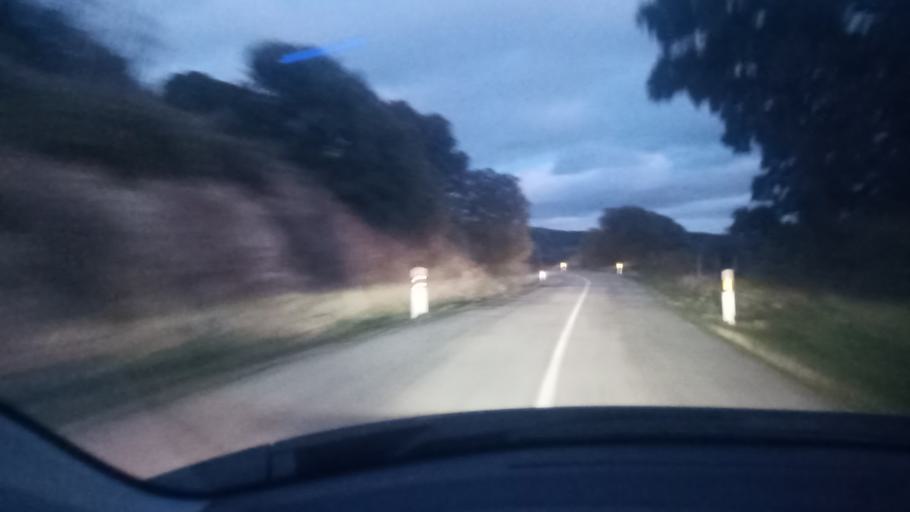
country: ES
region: Madrid
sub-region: Provincia de Madrid
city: Colmenar del Arroyo
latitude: 40.4452
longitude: -4.2372
